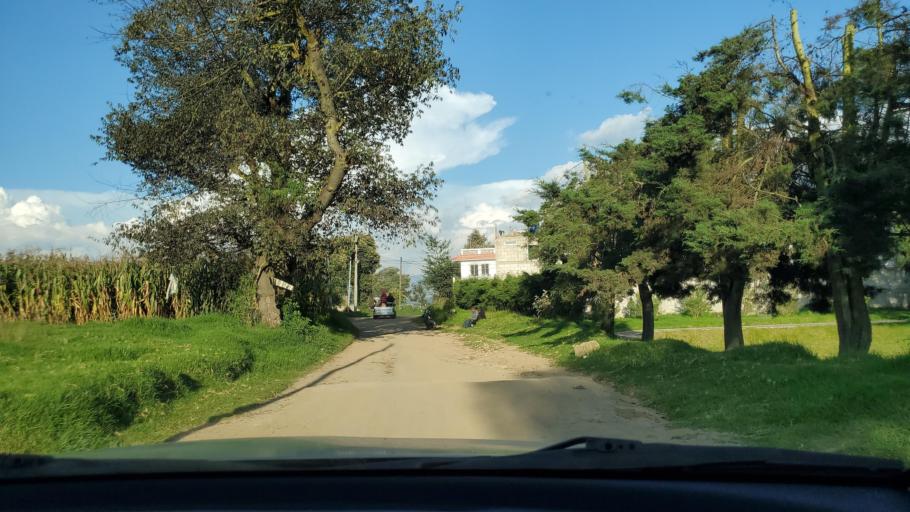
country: GT
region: Quetzaltenango
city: Quetzaltenango
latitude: 14.8366
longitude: -91.5488
